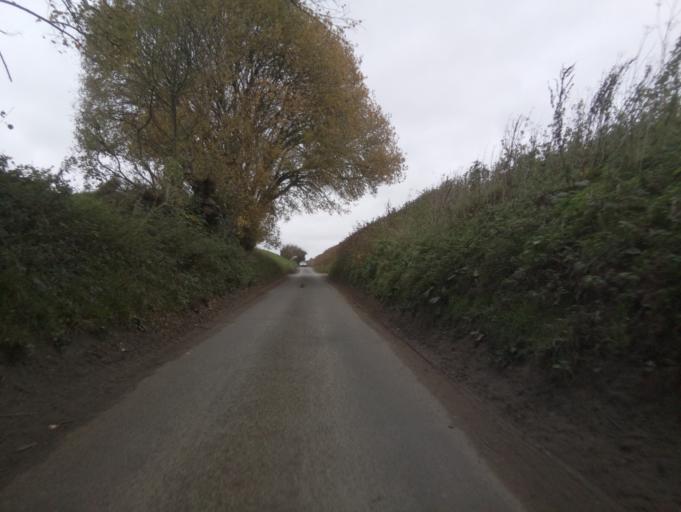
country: GB
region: England
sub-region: Somerset
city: South Petherton
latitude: 50.9428
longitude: -2.8509
